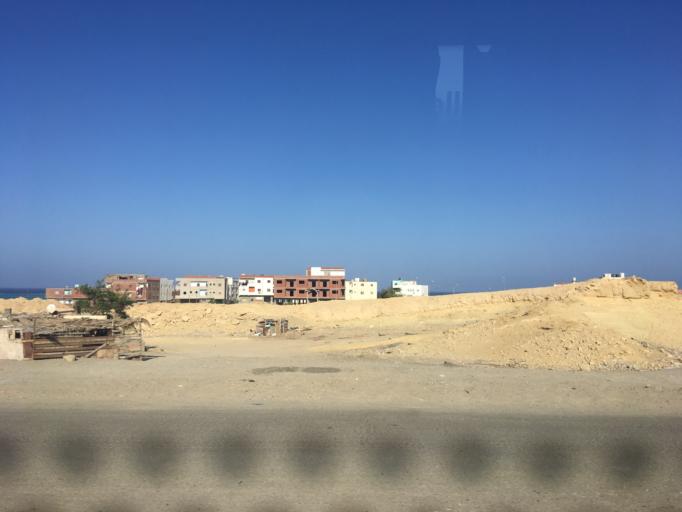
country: EG
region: Red Sea
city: Marsa Alam
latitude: 25.0789
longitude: 34.8828
